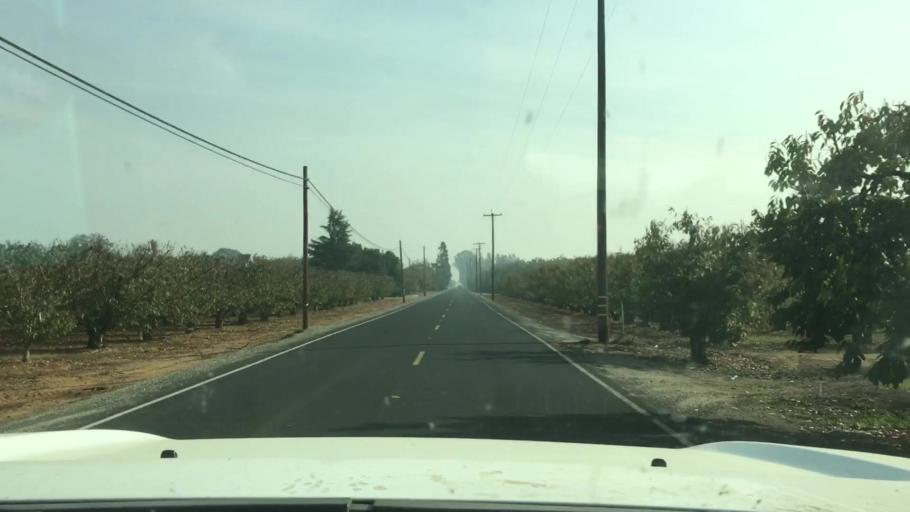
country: US
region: California
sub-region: San Joaquin County
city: Morada
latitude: 38.0290
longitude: -121.1849
